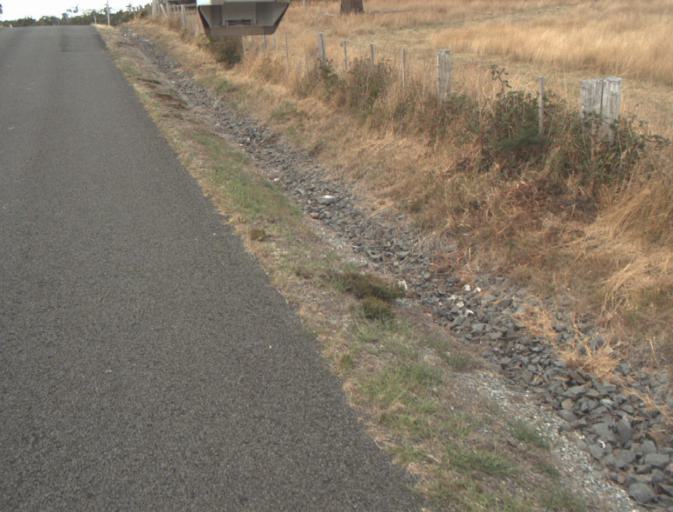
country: AU
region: Tasmania
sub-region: Launceston
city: Mayfield
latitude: -41.2914
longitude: 147.0139
